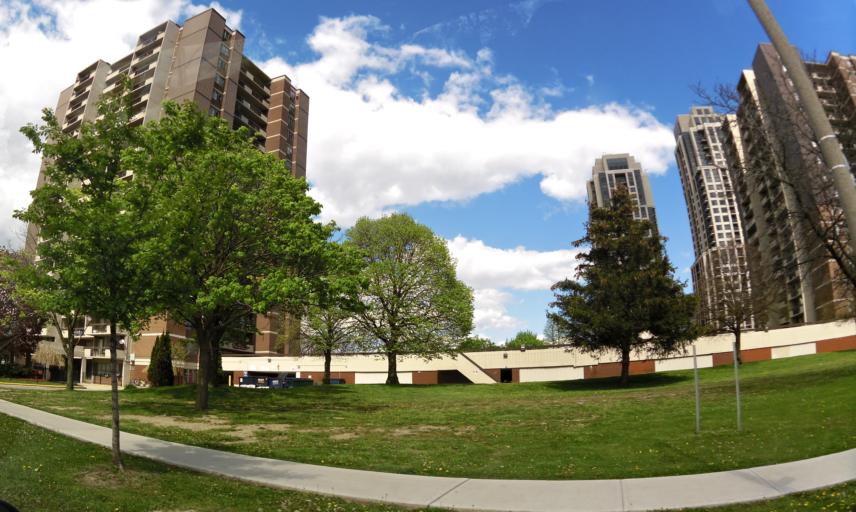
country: CA
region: Ontario
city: Etobicoke
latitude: 43.6403
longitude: -79.5651
